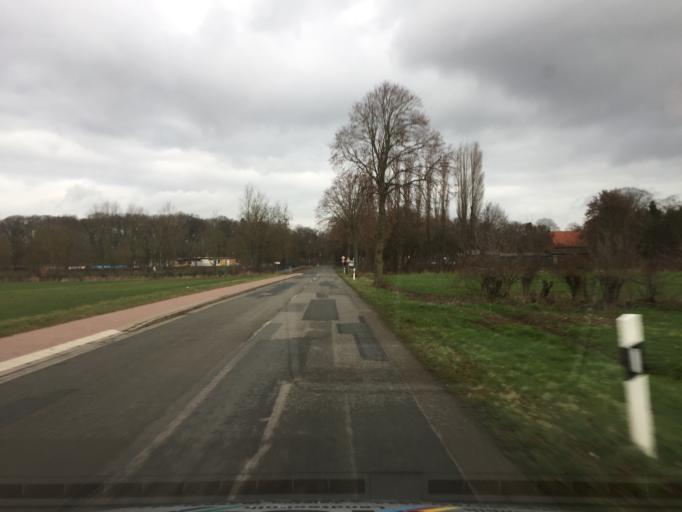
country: DE
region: Lower Saxony
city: Stolzenau
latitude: 52.5050
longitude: 9.0735
